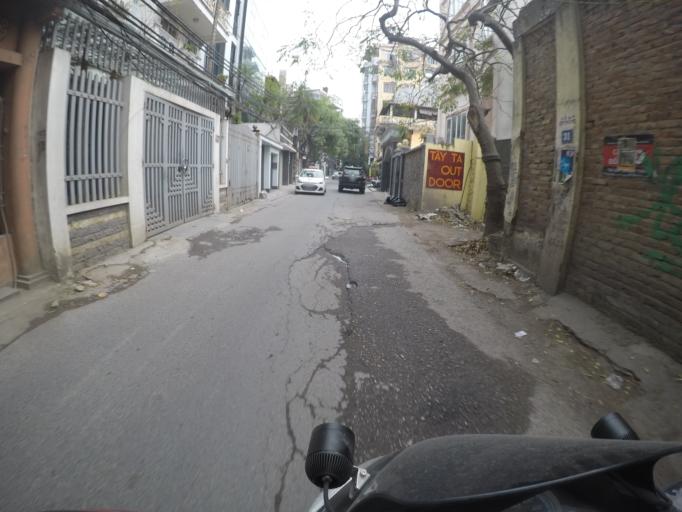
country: VN
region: Ha Noi
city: Tay Ho
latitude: 21.0701
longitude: 105.8232
